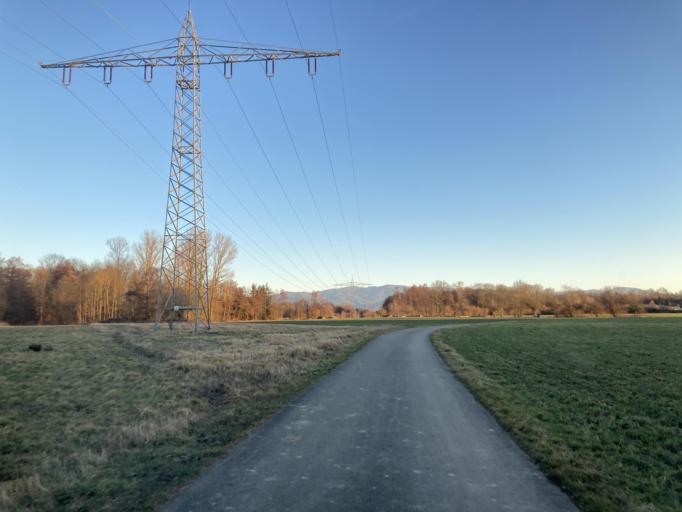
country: DE
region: Baden-Wuerttemberg
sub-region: Freiburg Region
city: Umkirch
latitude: 48.0483
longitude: 7.7684
